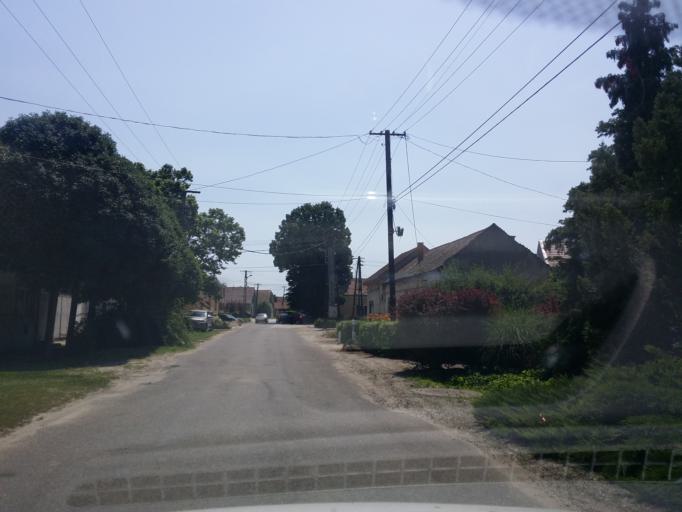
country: HU
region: Bacs-Kiskun
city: Tiszaalpar
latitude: 46.8235
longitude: 19.9899
